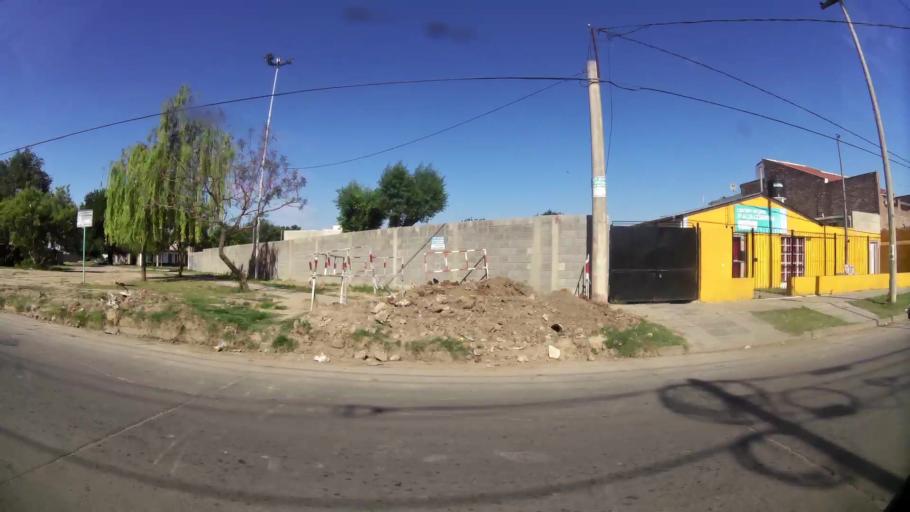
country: AR
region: Cordoba
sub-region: Departamento de Capital
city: Cordoba
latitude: -31.3775
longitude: -64.1838
